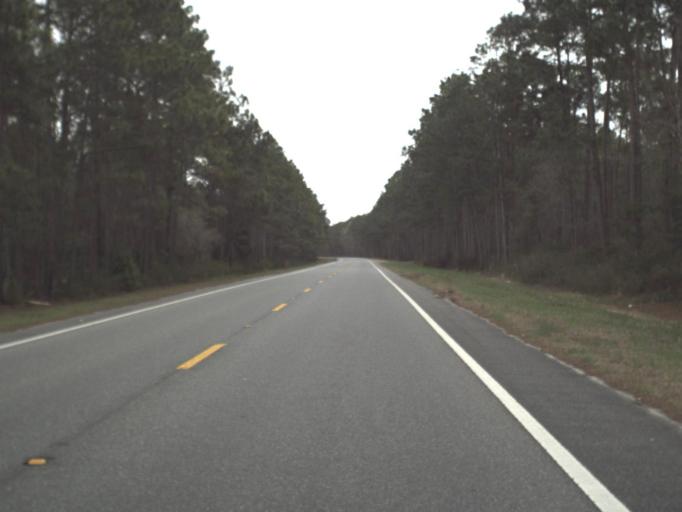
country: US
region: Florida
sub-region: Gadsden County
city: Midway
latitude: 30.3889
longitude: -84.6217
